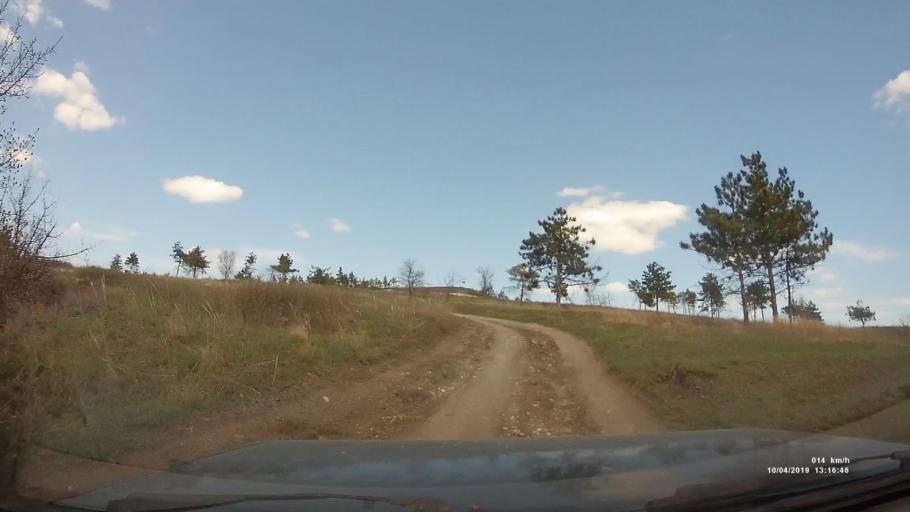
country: RU
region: Rostov
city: Masalovka
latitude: 48.4216
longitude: 40.2554
